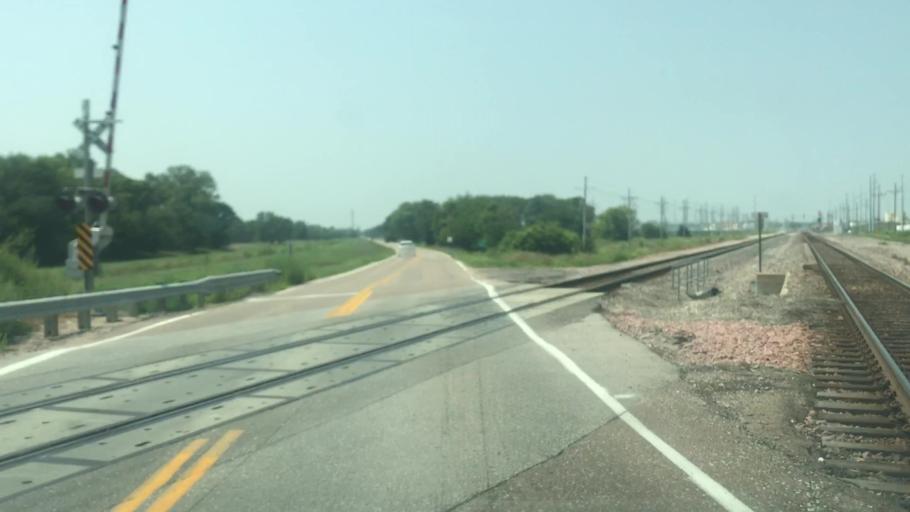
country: US
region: Nebraska
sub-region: Hall County
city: Grand Island
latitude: 40.9162
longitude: -98.3073
